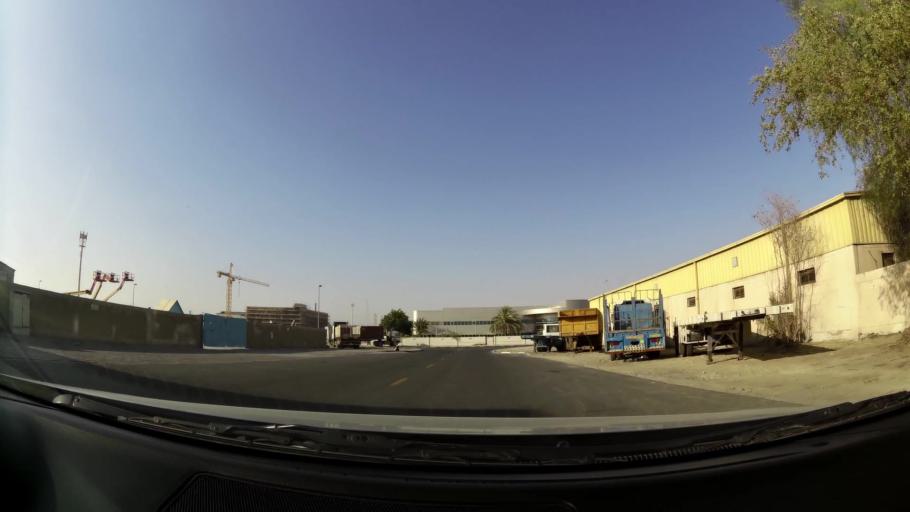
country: AE
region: Dubai
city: Dubai
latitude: 25.1277
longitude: 55.2423
